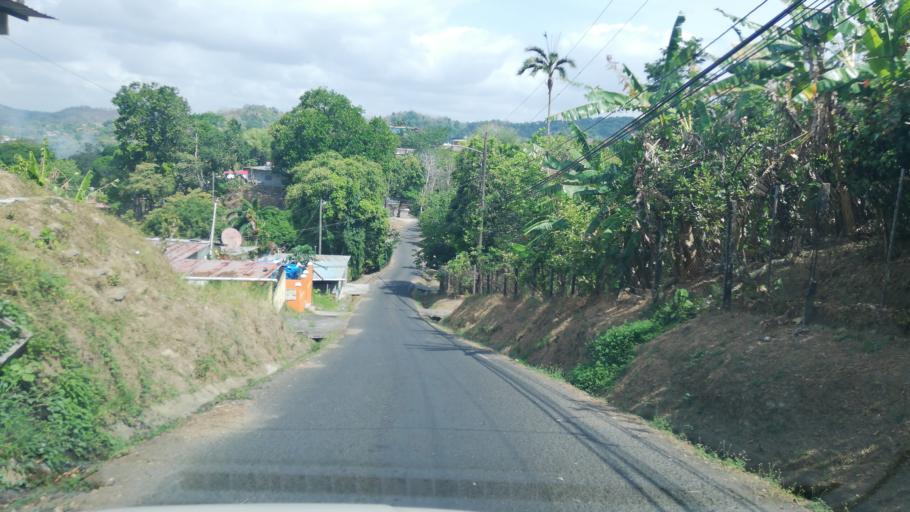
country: PA
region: Panama
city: Alcalde Diaz
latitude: 9.1213
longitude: -79.5639
